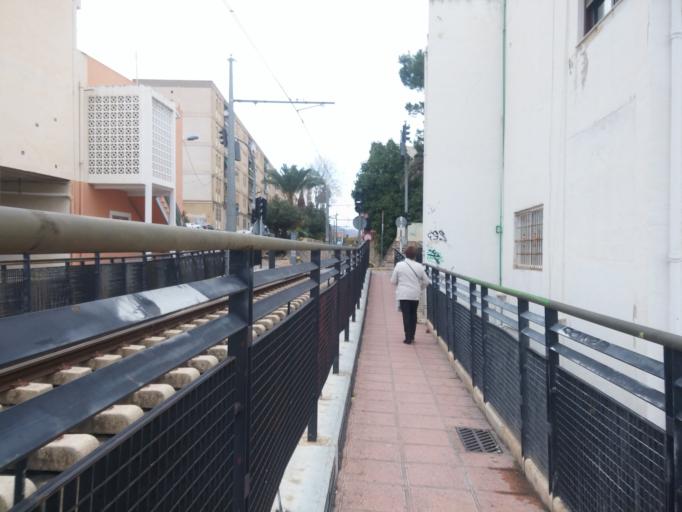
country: ES
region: Valencia
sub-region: Provincia de Alicante
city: Villajoyosa
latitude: 38.5074
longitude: -0.2346
